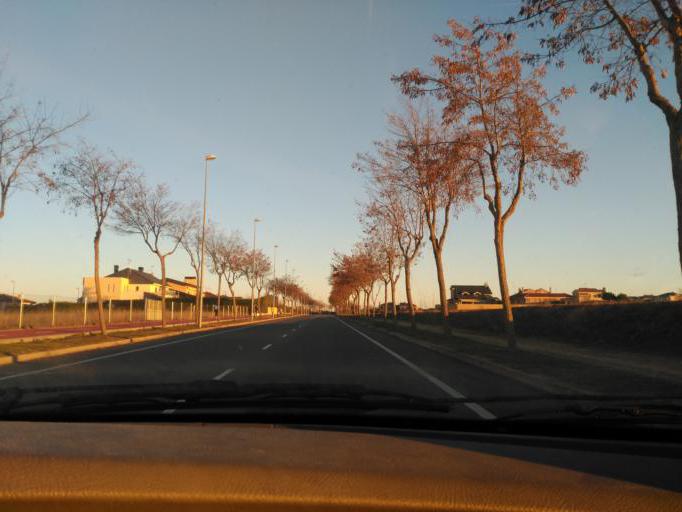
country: ES
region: Castille and Leon
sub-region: Provincia de Salamanca
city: Carbajosa de la Sagrada
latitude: 40.9368
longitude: -5.6352
